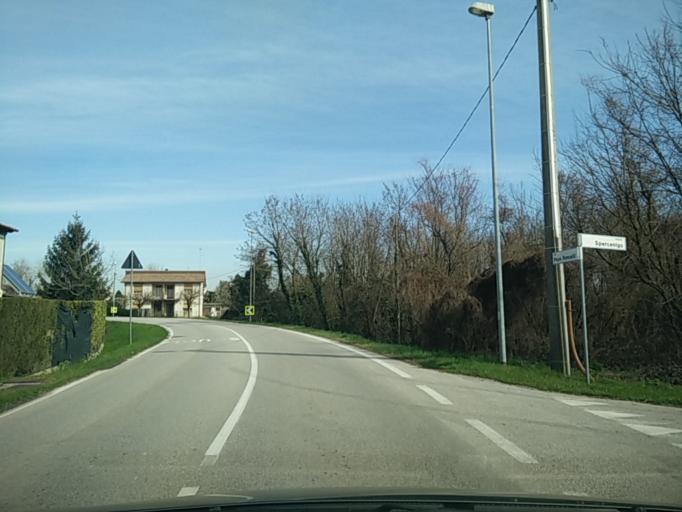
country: IT
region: Veneto
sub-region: Provincia di Treviso
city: Mignagola
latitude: 45.6902
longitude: 12.3242
